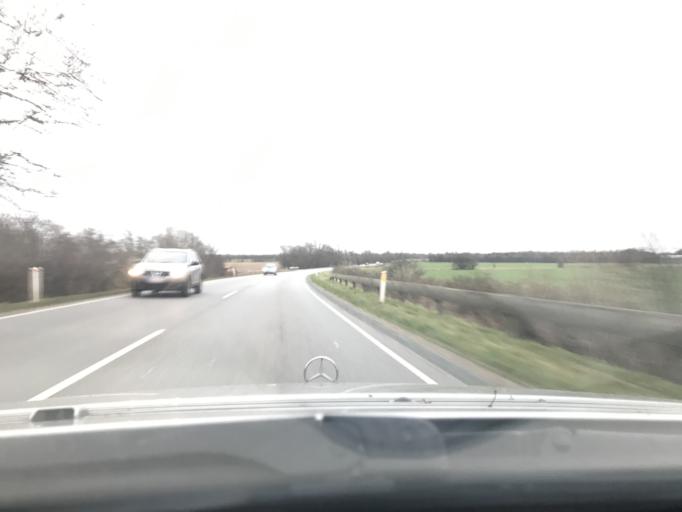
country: DK
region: South Denmark
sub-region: Aabenraa Kommune
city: Rodekro
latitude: 55.0836
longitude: 9.2173
